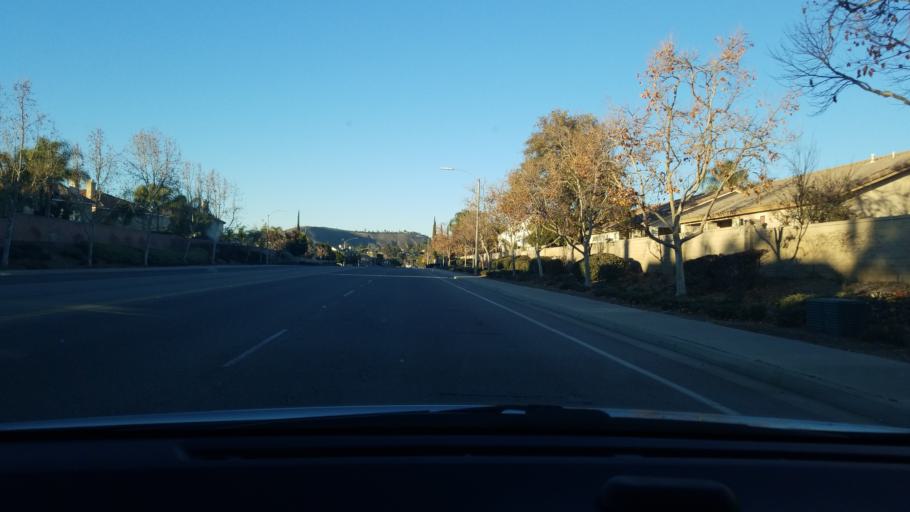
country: US
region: California
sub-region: Riverside County
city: Murrieta Hot Springs
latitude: 33.5513
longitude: -117.1575
